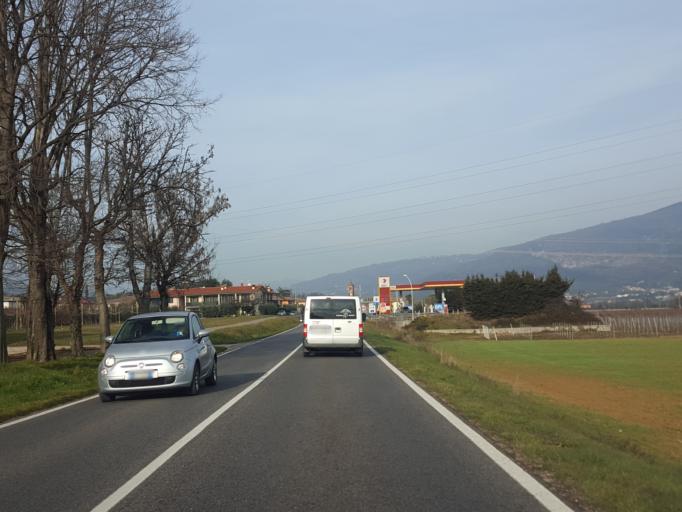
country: IT
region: Veneto
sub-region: Provincia di Verona
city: Costermano
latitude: 45.5681
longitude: 10.7615
